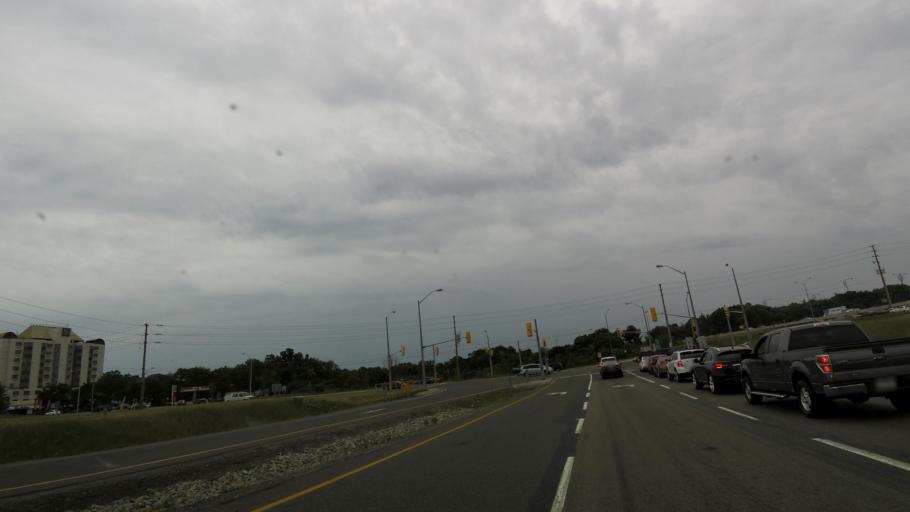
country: CA
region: Ontario
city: Oakville
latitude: 43.4092
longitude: -79.7380
